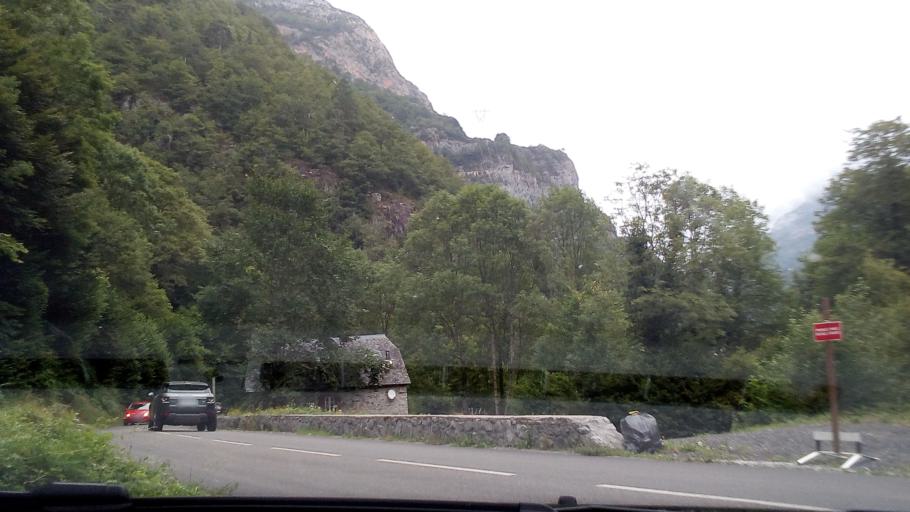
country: FR
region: Aquitaine
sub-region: Departement des Pyrenees-Atlantiques
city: Laruns
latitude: 42.9295
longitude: -0.4482
